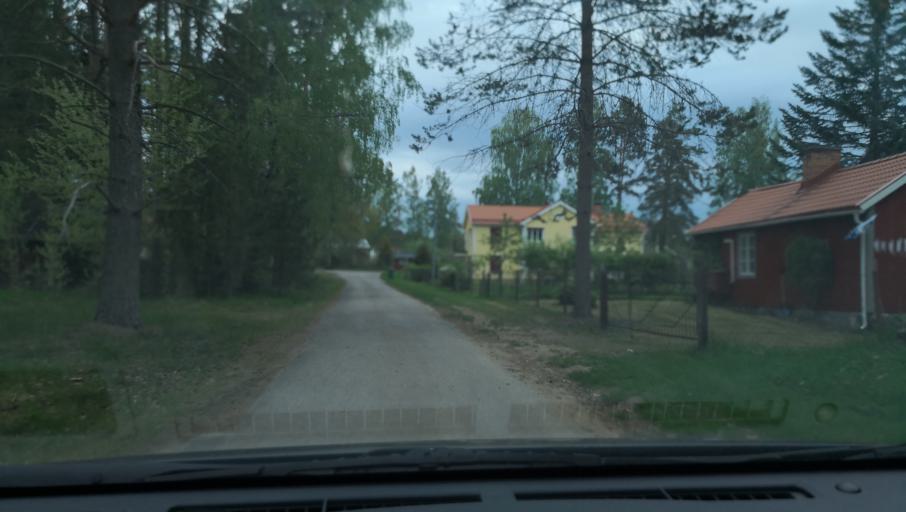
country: SE
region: Vaestmanland
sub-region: Skinnskattebergs Kommun
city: Skinnskatteberg
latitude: 59.8062
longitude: 15.5513
